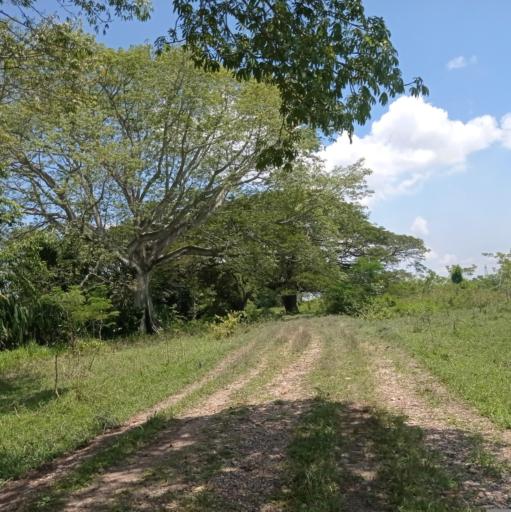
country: CO
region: Santander
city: Barrancabermeja
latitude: 7.1022
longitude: -73.8787
